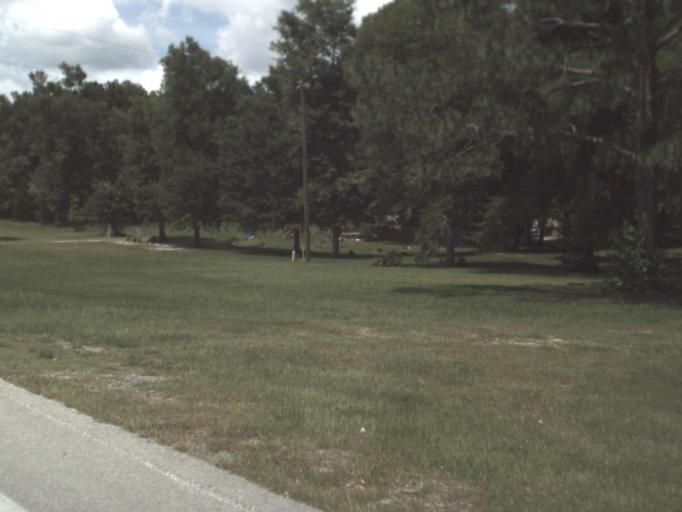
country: US
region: Florida
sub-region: Alachua County
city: Newberry
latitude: 29.6847
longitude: -82.6070
